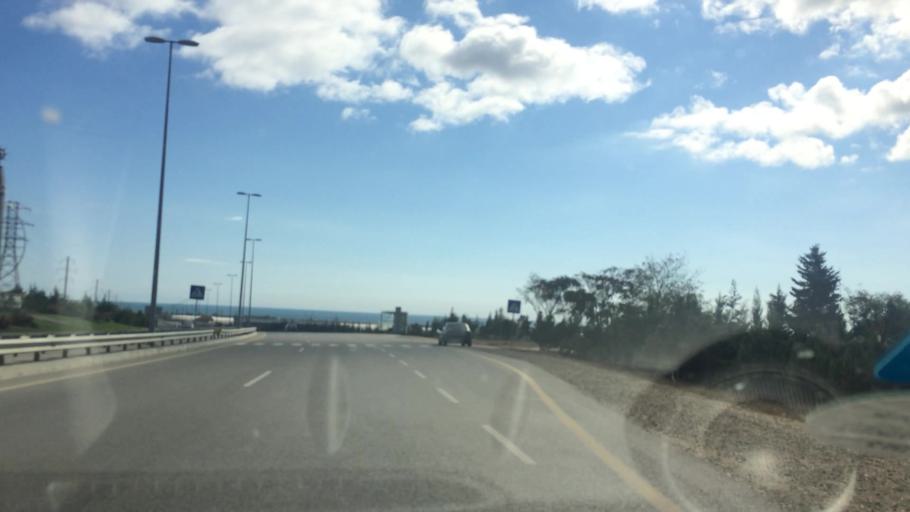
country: AZ
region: Baki
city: Zyrya
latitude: 40.4015
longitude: 50.3099
